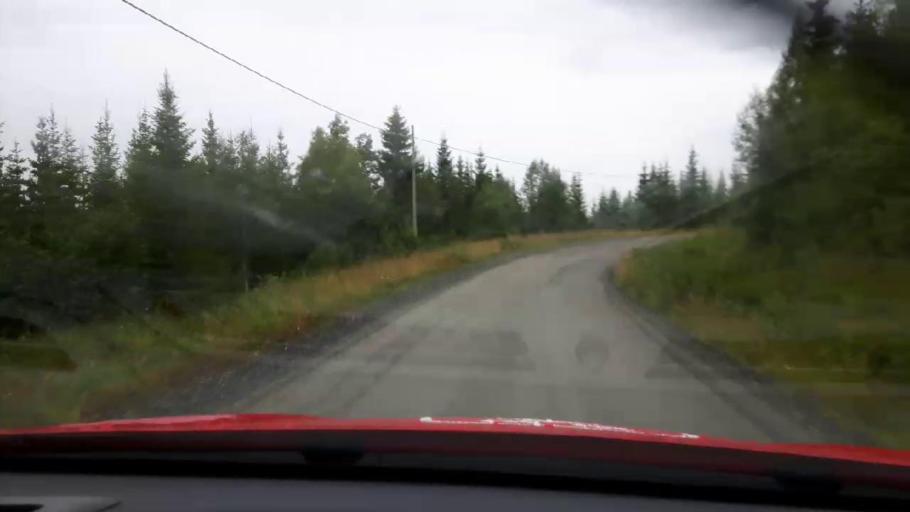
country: SE
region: Jaemtland
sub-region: Are Kommun
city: Are
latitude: 63.4215
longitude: 12.8219
